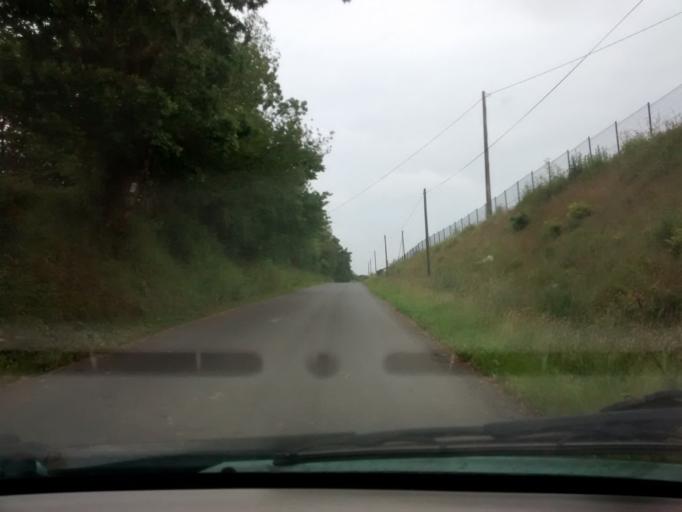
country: FR
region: Lower Normandy
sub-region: Departement de la Manche
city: Saint-Lo
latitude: 49.0980
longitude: -1.0656
